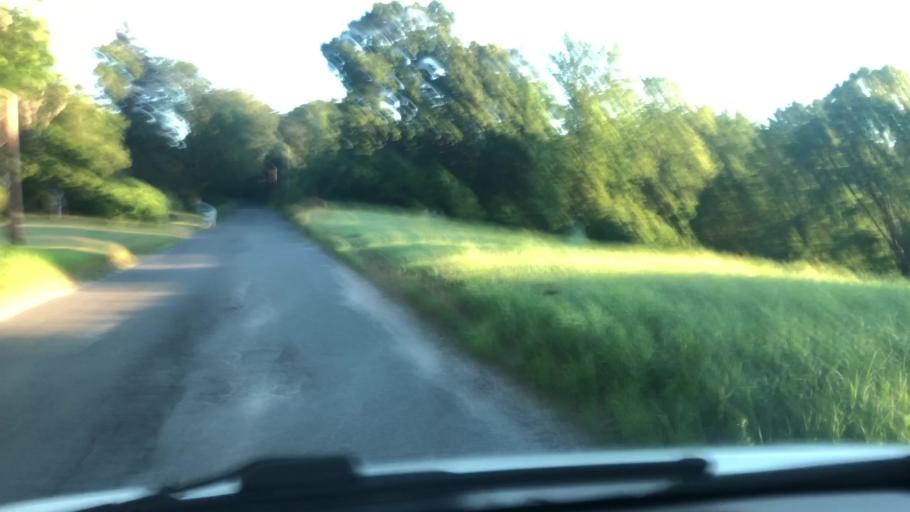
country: US
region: Massachusetts
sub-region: Hampshire County
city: Southampton
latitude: 42.2479
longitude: -72.7136
